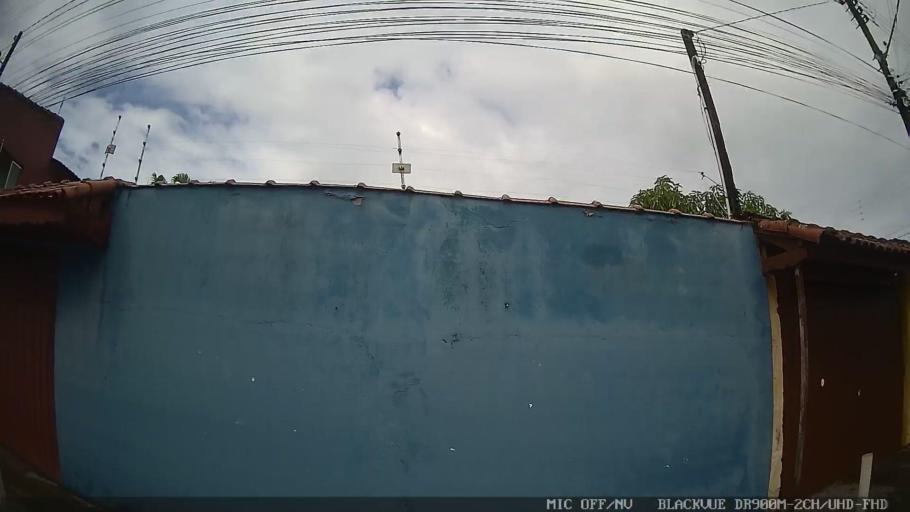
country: BR
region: Sao Paulo
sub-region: Itanhaem
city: Itanhaem
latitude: -24.1724
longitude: -46.7823
